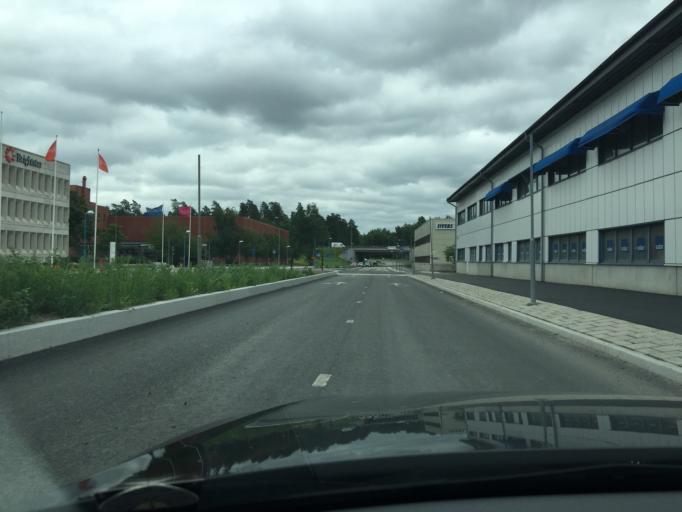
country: SE
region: Stockholm
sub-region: Stockholms Kommun
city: Kista
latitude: 59.4021
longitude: 17.9603
